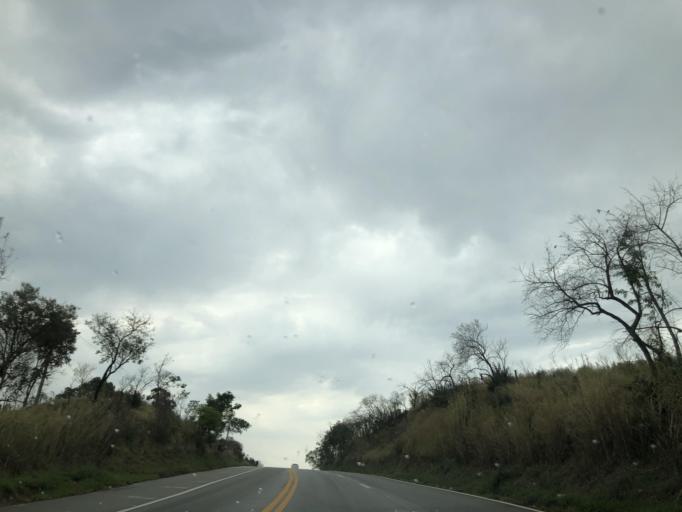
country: BR
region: Sao Paulo
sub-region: Salto De Pirapora
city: Salto de Pirapora
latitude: -23.6910
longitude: -47.6065
